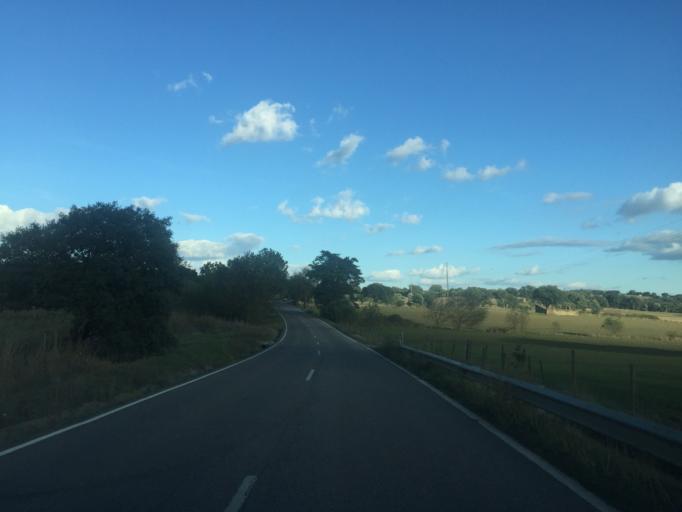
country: PT
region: Portalegre
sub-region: Alter do Chao
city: Alter do Chao
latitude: 39.1957
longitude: -7.6856
